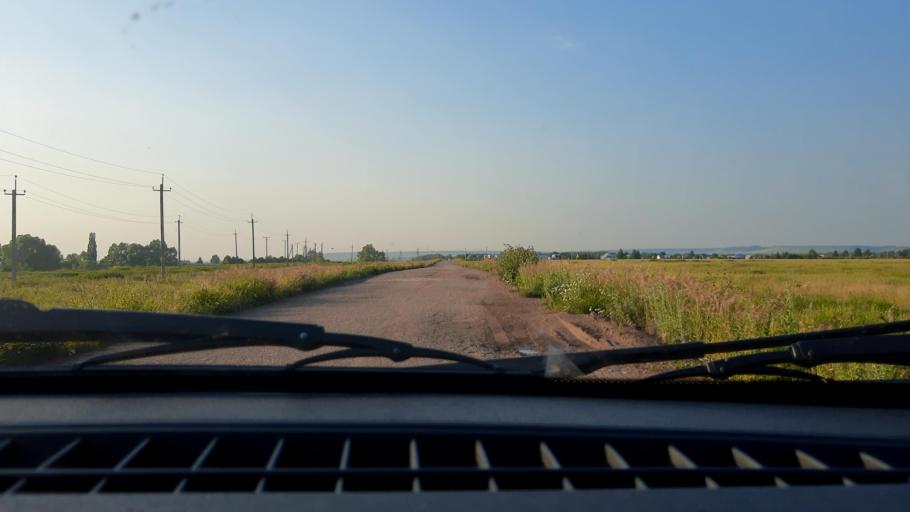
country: RU
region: Bashkortostan
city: Asanovo
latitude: 54.9091
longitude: 55.6267
